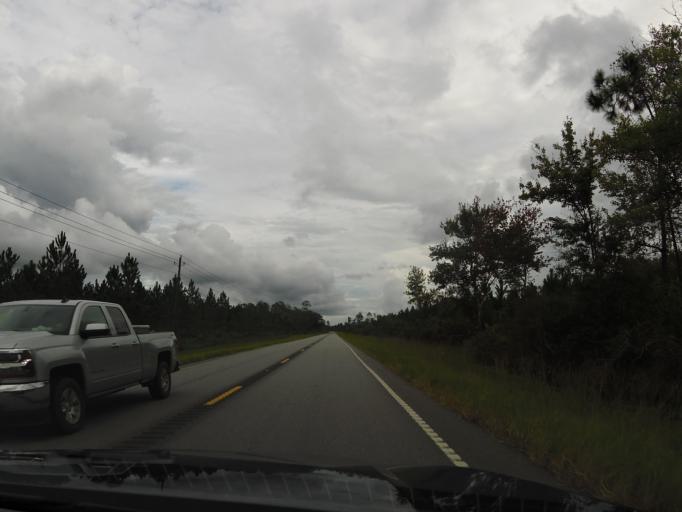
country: US
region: Florida
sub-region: Baker County
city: Macclenny
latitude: 30.5218
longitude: -82.1501
